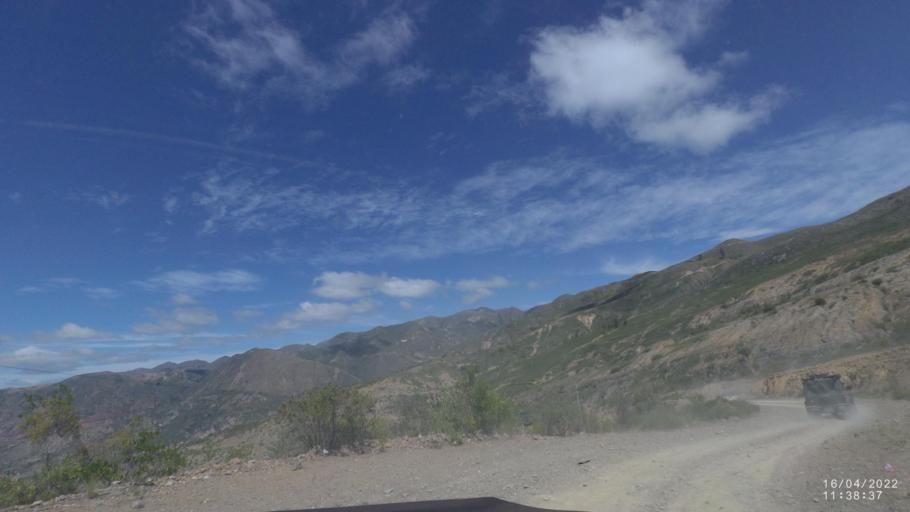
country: BO
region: Cochabamba
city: Mizque
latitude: -17.9645
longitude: -65.6371
